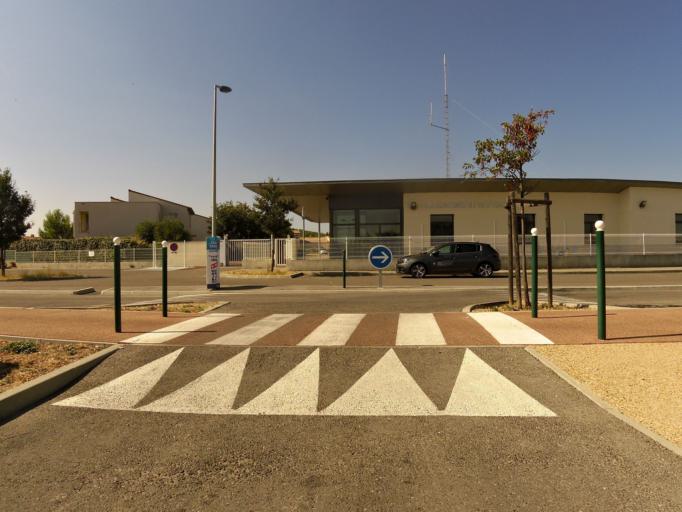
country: FR
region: Languedoc-Roussillon
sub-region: Departement du Gard
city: Calvisson
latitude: 43.7883
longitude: 4.2042
